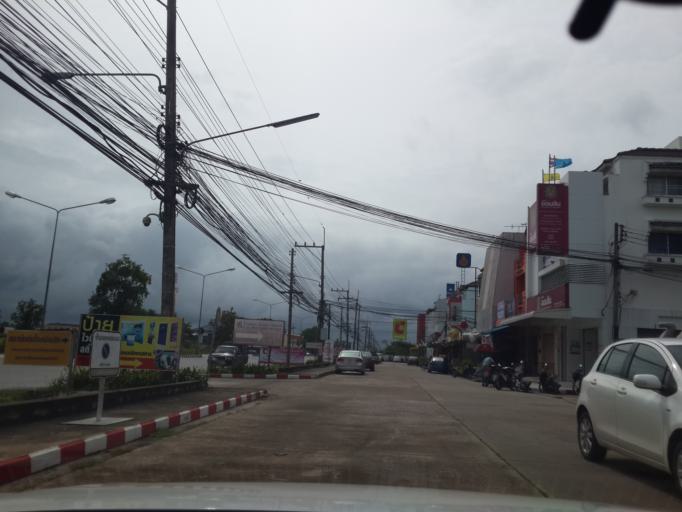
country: TH
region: Pattani
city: Pattani
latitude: 6.8623
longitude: 101.2345
